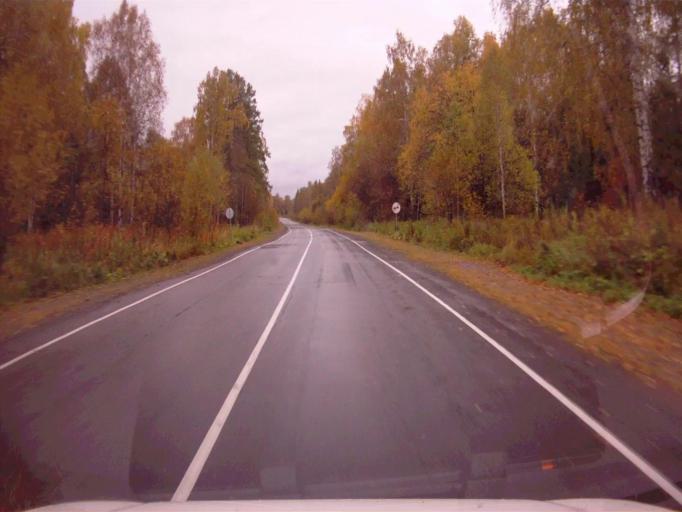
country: RU
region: Chelyabinsk
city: Nizhniy Ufaley
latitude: 56.0652
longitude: 60.0018
